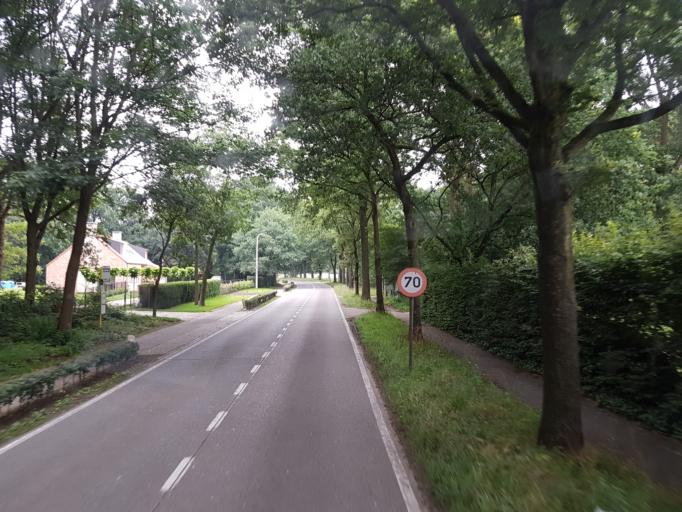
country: BE
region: Flanders
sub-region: Provincie Antwerpen
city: Schilde
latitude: 51.2181
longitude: 4.5998
